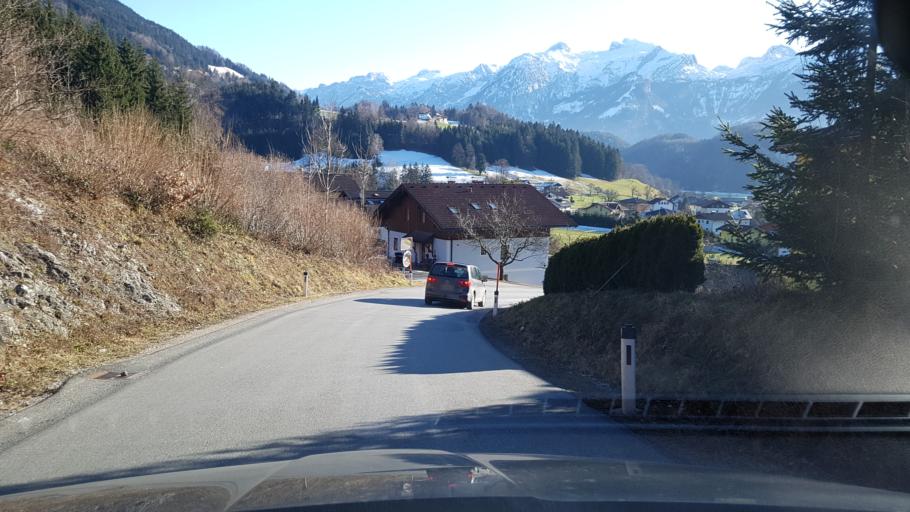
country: AT
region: Salzburg
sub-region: Politischer Bezirk Hallein
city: Golling an der Salzach
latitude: 47.6191
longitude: 13.1732
